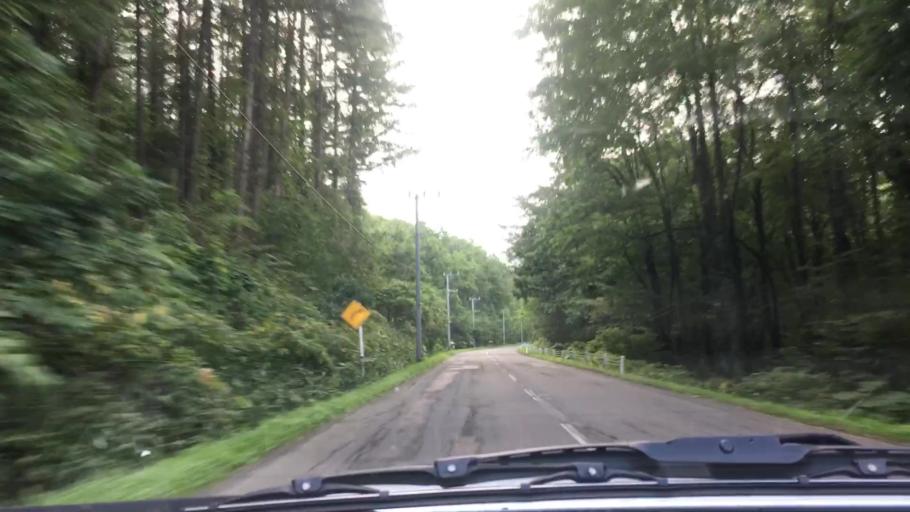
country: JP
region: Hokkaido
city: Otofuke
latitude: 43.1446
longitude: 142.8773
